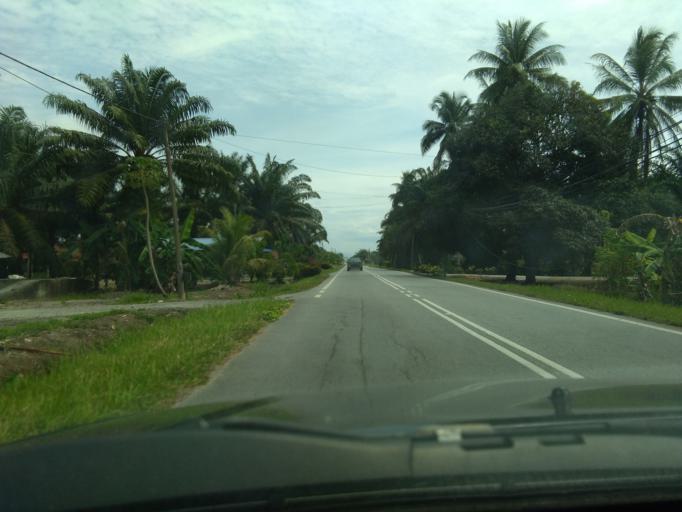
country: MY
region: Perak
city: Bagan Serai
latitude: 5.0569
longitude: 100.5933
